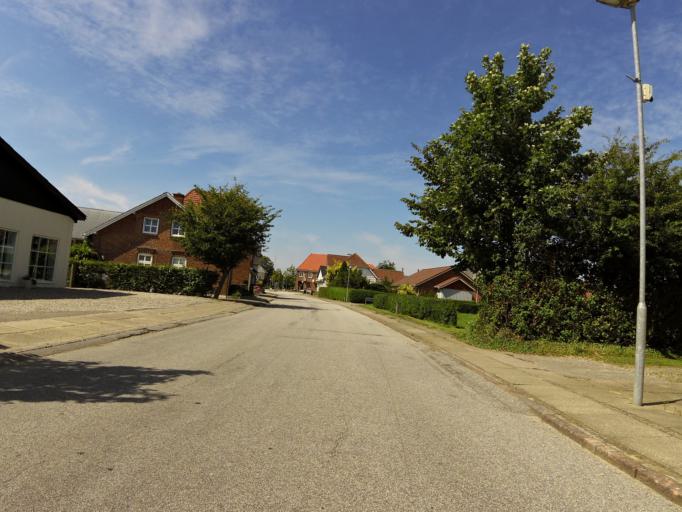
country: DK
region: South Denmark
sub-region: Haderslev Kommune
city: Gram
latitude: 55.2469
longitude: 8.9712
